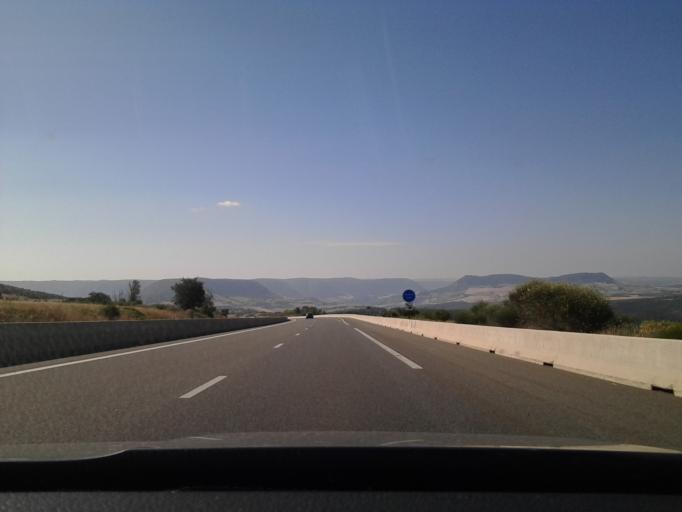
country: FR
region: Midi-Pyrenees
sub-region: Departement de l'Aveyron
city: Severac-le-Chateau
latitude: 44.2388
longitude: 3.0584
